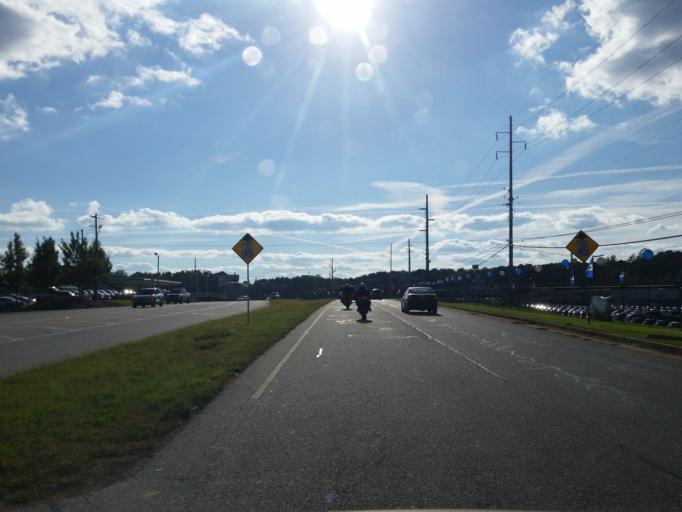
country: US
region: Georgia
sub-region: Paulding County
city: Hiram
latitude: 33.9182
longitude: -84.7676
